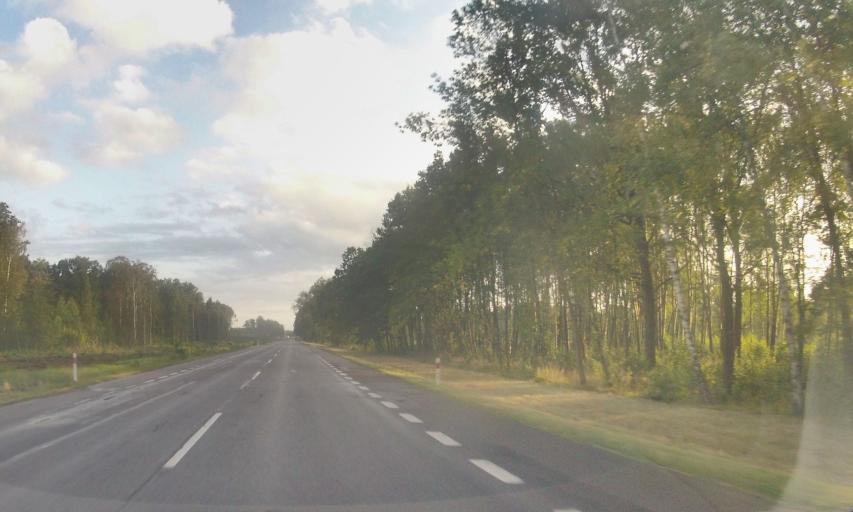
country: PL
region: Masovian Voivodeship
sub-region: Powiat ciechanowski
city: Glinojeck
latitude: 52.7465
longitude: 20.3161
